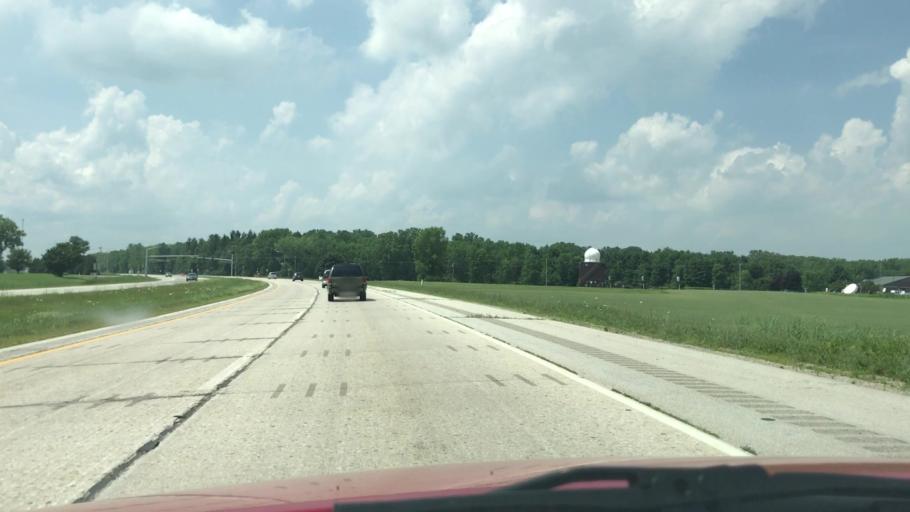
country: US
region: Wisconsin
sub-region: Brown County
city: Ashwaubenon
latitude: 44.4964
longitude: -88.1090
